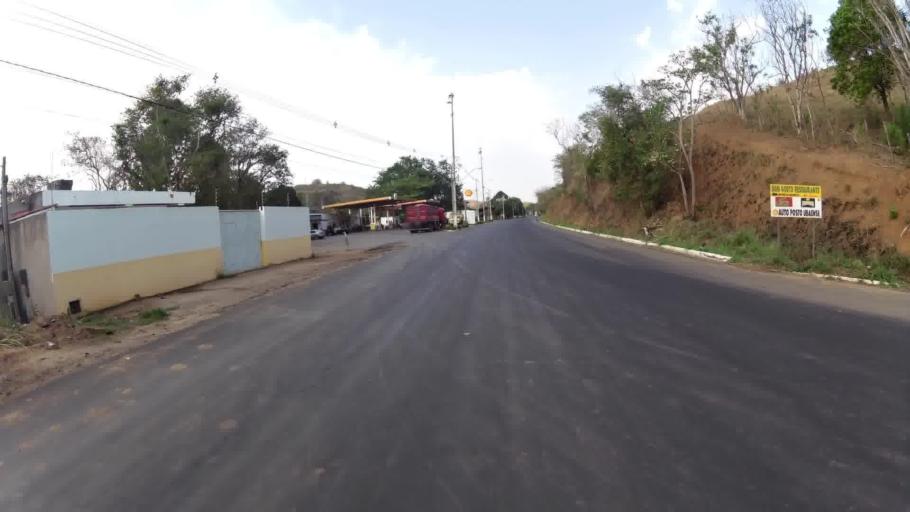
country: BR
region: Rio de Janeiro
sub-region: Itaperuna
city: Itaperuna
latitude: -21.3677
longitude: -41.9390
